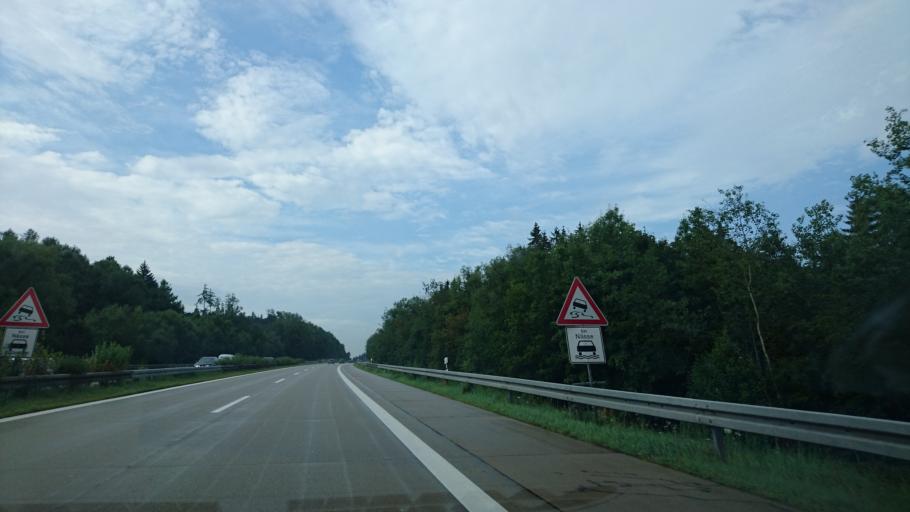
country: DE
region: Bavaria
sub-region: Lower Bavaria
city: Bad Abbach
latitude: 48.9095
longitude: 12.0859
